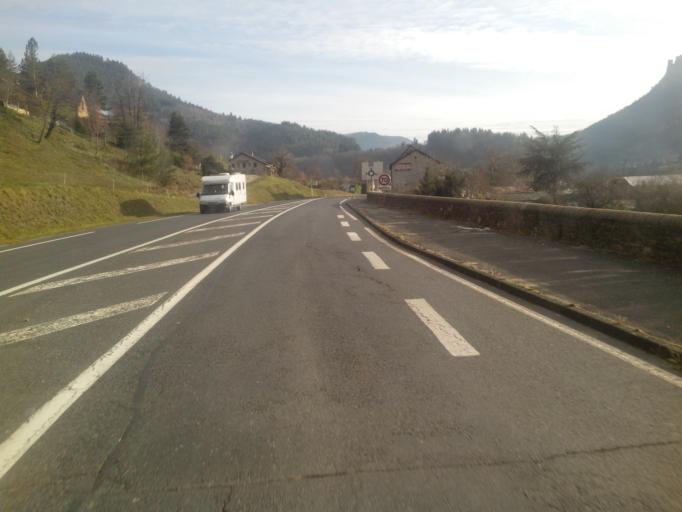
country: FR
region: Languedoc-Roussillon
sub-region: Departement de la Lozere
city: Florac
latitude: 44.3423
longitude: 3.5841
